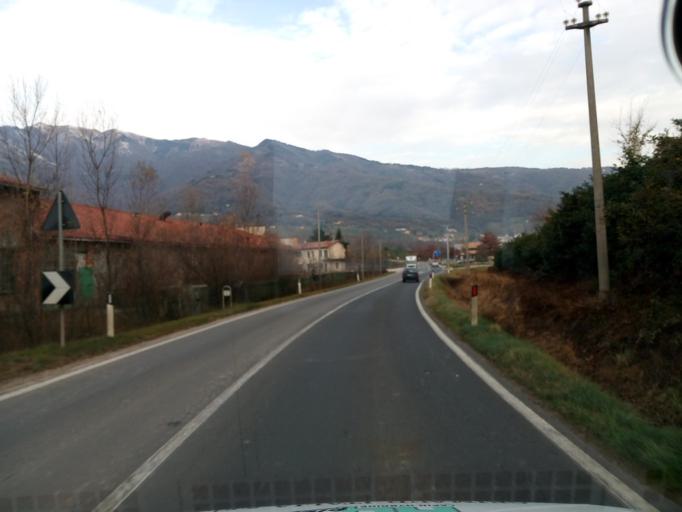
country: IT
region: Veneto
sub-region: Provincia di Treviso
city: Possagno
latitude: 45.8461
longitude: 11.8896
